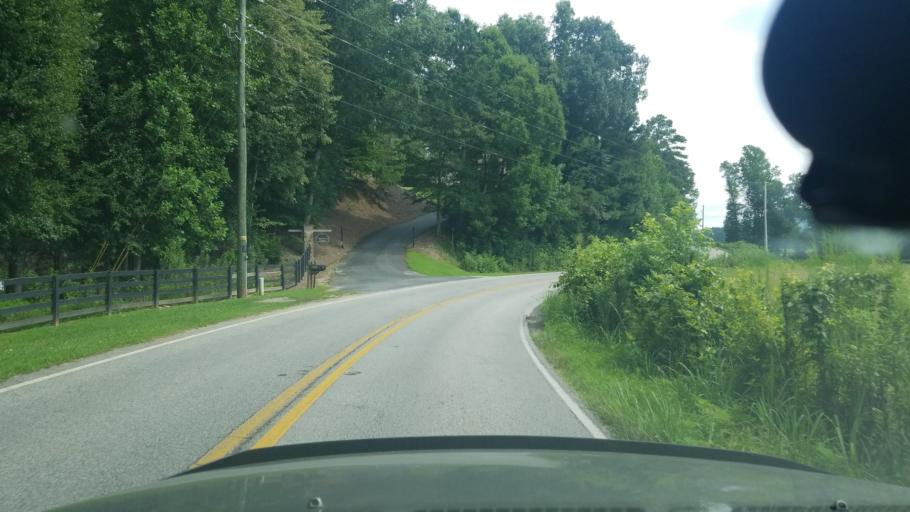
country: US
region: Georgia
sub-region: Forsyth County
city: Cumming
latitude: 34.2753
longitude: -84.1521
